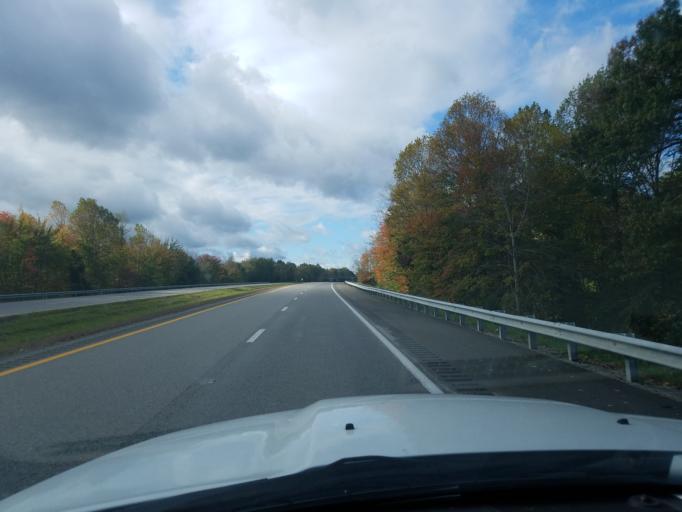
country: US
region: Kentucky
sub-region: Russell County
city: Russell Springs
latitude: 37.0577
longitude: -85.0594
